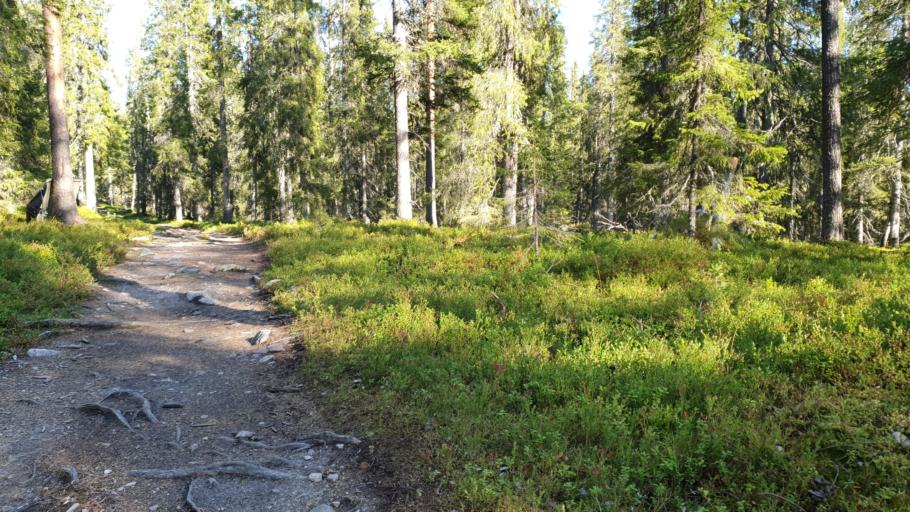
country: FI
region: Lapland
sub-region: Tunturi-Lappi
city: Kolari
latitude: 67.5986
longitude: 24.2799
